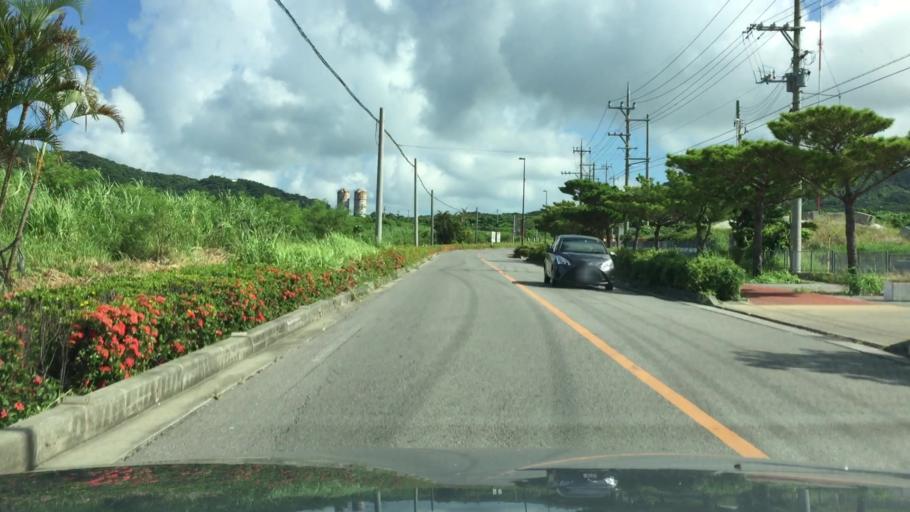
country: JP
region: Okinawa
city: Ishigaki
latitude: 24.3610
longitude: 124.1570
